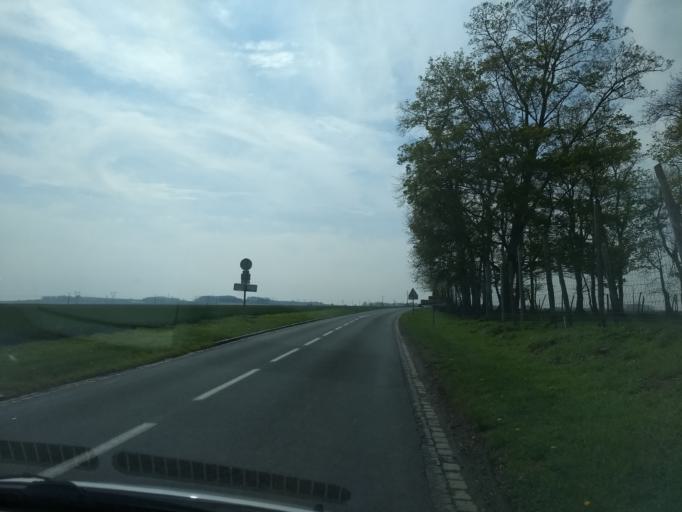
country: FR
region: Nord-Pas-de-Calais
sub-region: Departement du Nord
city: Cantin
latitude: 50.3251
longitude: 3.1466
